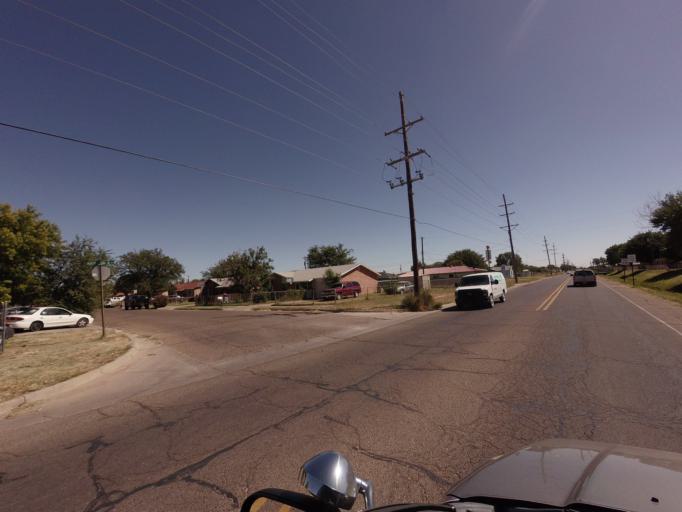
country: US
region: New Mexico
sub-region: Curry County
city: Clovis
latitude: 34.4096
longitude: -103.2317
